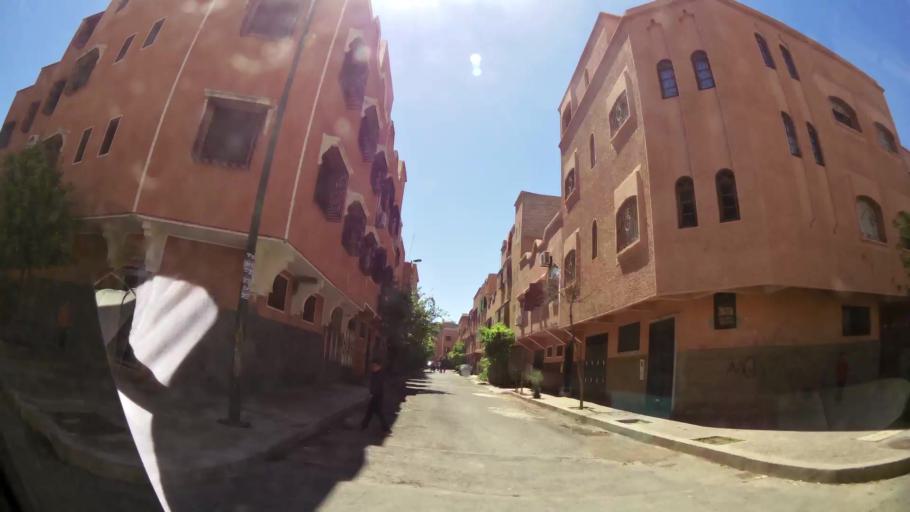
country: MA
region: Marrakech-Tensift-Al Haouz
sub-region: Marrakech
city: Marrakesh
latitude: 31.6560
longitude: -7.9874
